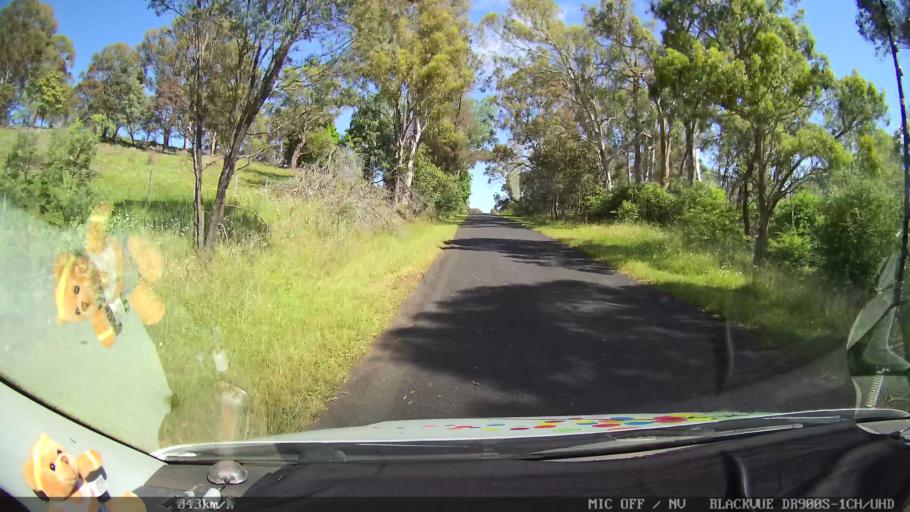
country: AU
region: New South Wales
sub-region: Guyra
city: Guyra
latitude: -30.1096
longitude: 151.6811
